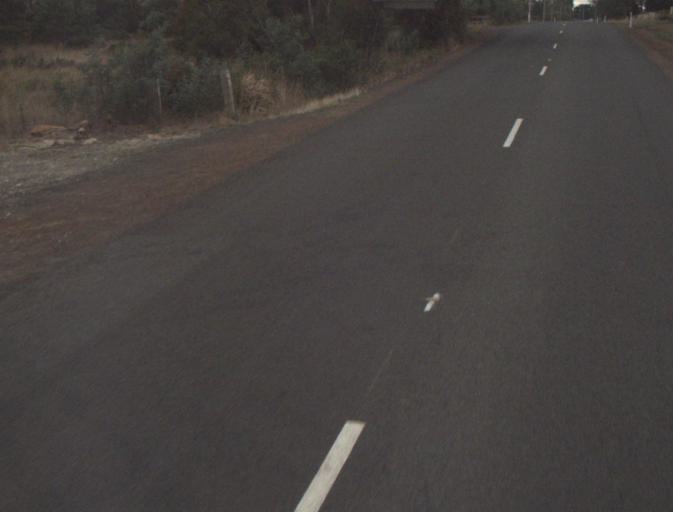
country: AU
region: Tasmania
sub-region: Launceston
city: Summerhill
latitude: -41.4970
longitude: 147.1836
